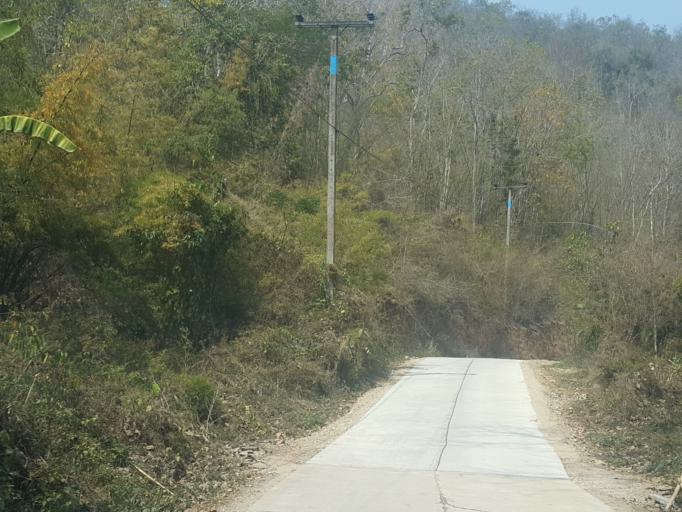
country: TH
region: Chiang Mai
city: Hang Dong
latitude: 18.7414
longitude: 98.8255
